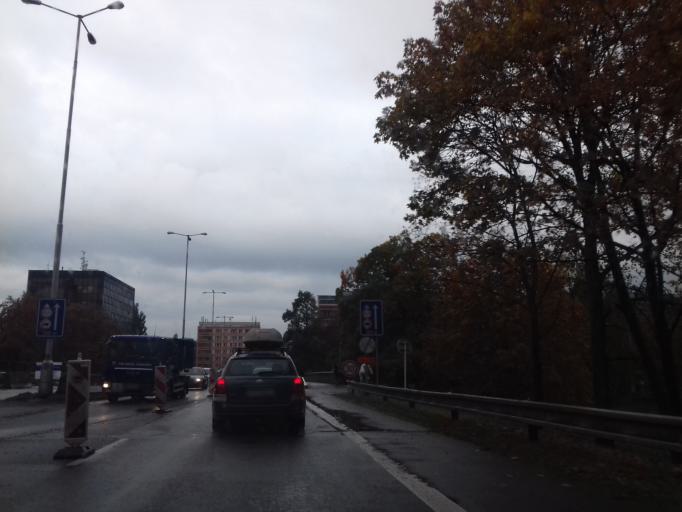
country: CZ
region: Kralovehradecky
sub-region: Okres Hradec Kralove
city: Hradec Kralove
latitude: 50.2173
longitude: 15.8263
